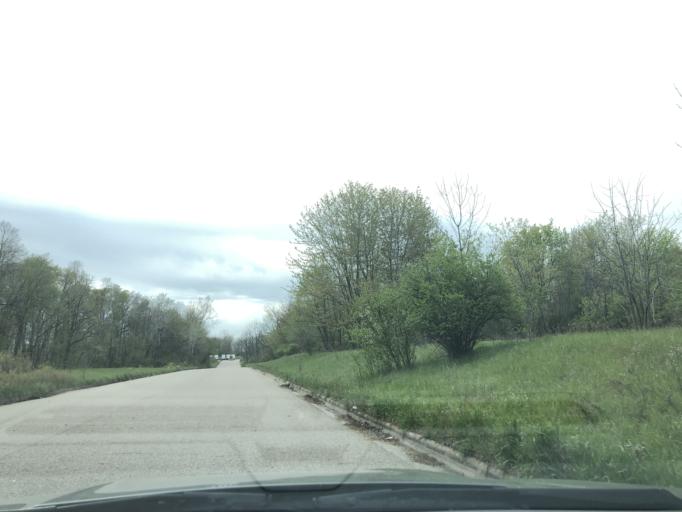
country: US
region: Michigan
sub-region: Eaton County
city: Waverly
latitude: 42.7078
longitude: -84.6484
